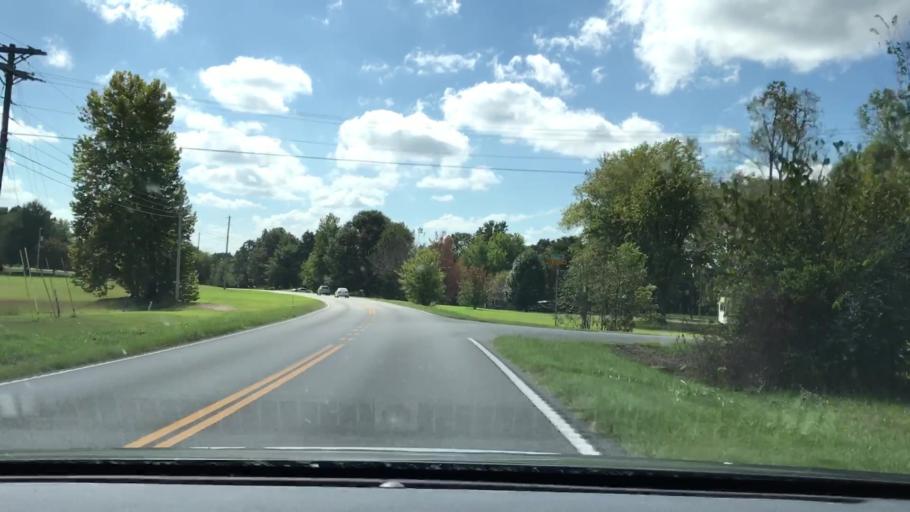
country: US
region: Kentucky
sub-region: McCracken County
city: Reidland
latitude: 36.9813
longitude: -88.5163
